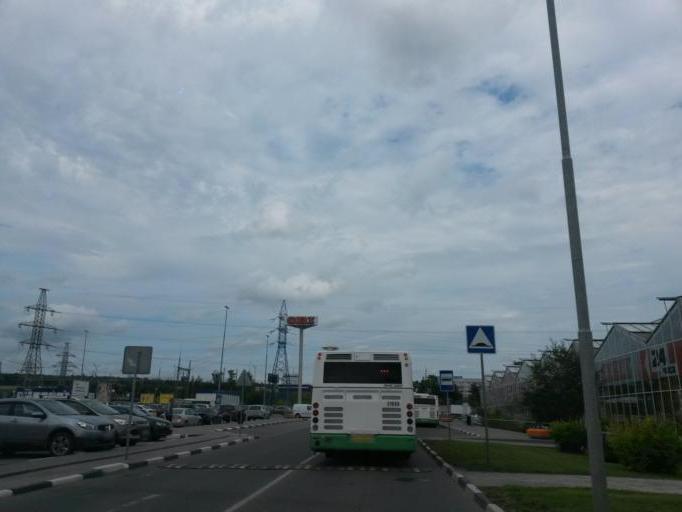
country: RU
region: Moscow
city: Tyoply Stan
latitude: 55.6026
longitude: 37.4970
